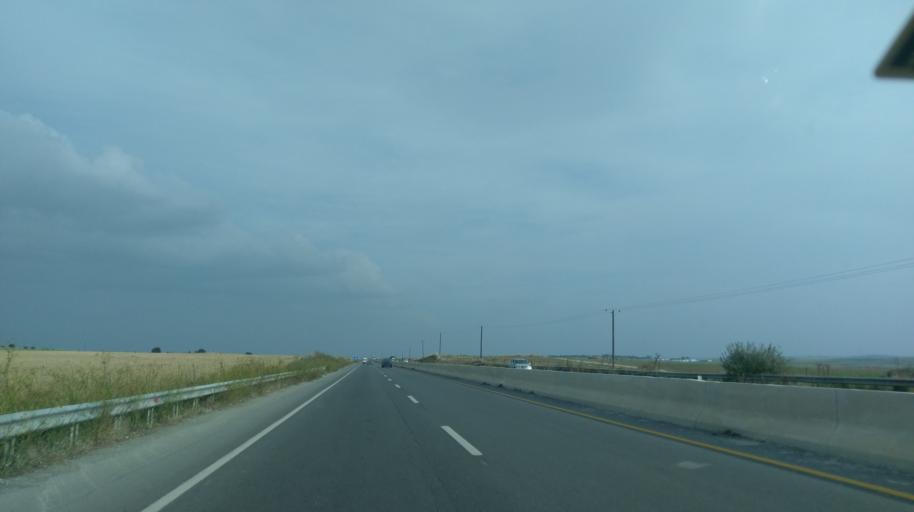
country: CY
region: Lefkosia
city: Mammari
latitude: 35.2118
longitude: 33.2097
